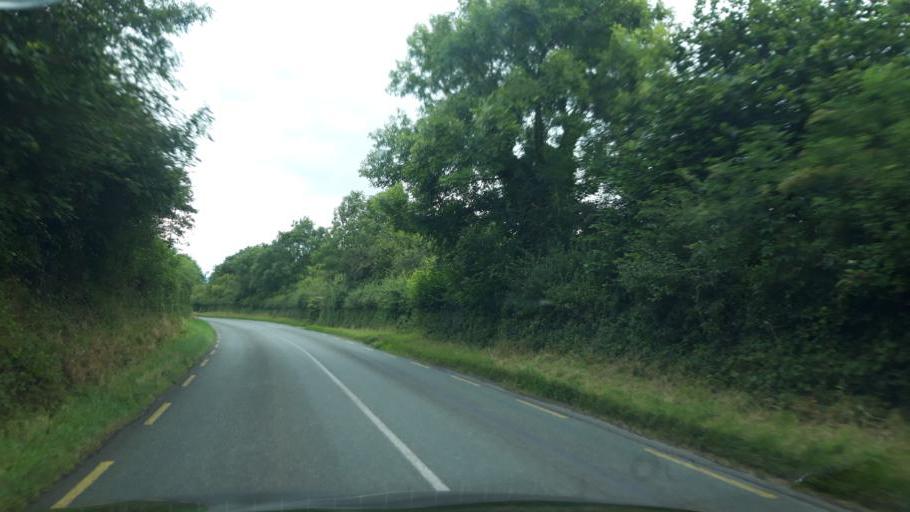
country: IE
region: Leinster
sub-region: Kilkenny
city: Ballyragget
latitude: 52.7962
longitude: -7.3149
